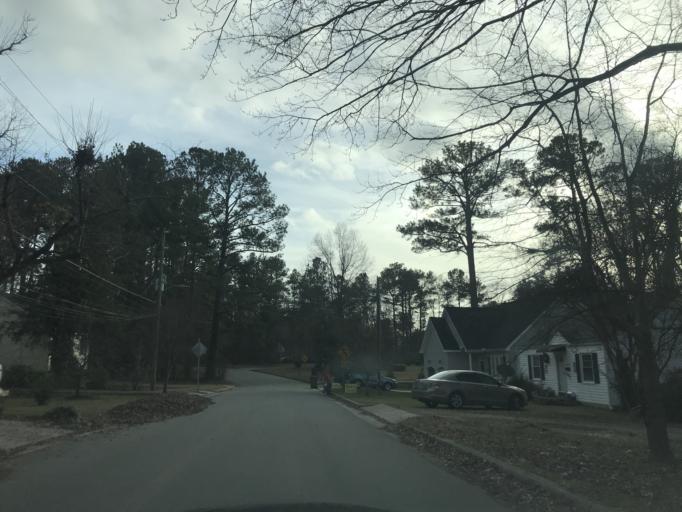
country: US
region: North Carolina
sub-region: Wake County
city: Raleigh
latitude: 35.7971
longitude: -78.6179
